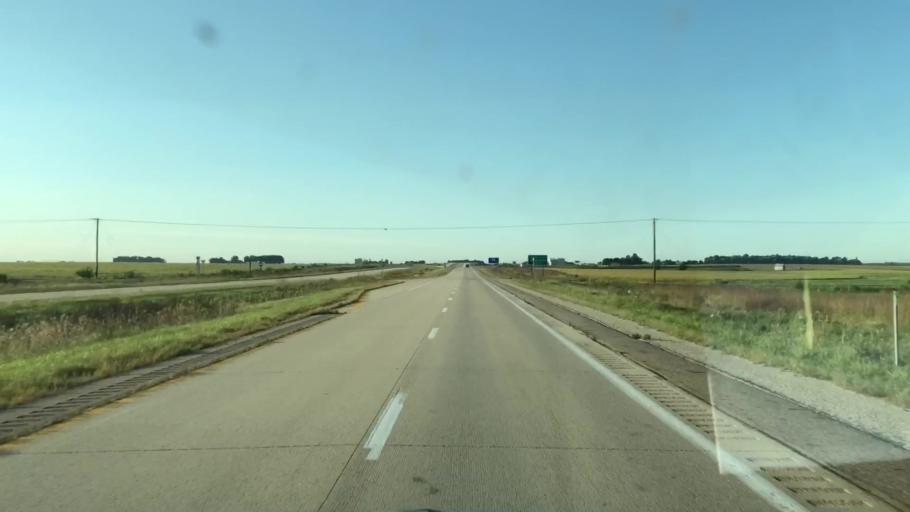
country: US
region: Iowa
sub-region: Osceola County
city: Sibley
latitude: 43.4483
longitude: -95.7135
